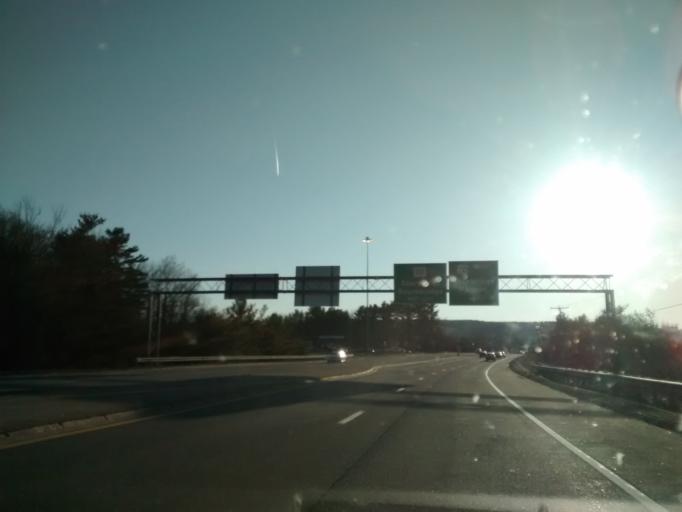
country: US
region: Massachusetts
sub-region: Worcester County
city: Sturbridge
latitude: 42.1128
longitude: -72.0844
